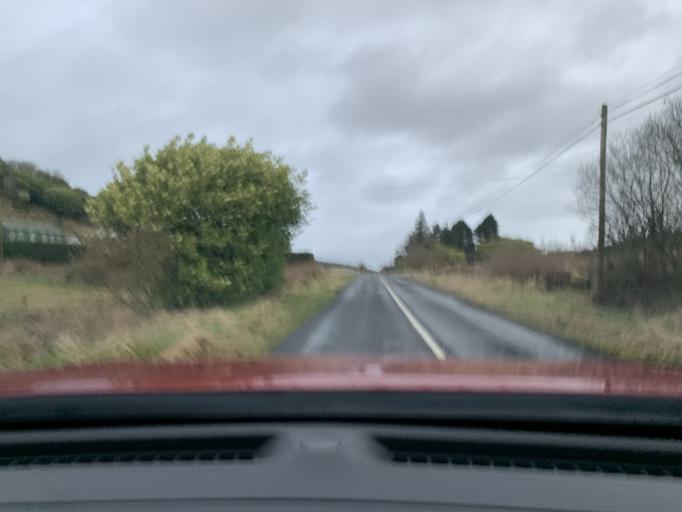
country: IE
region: Connaught
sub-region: Roscommon
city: Boyle
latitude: 53.9987
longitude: -8.3095
